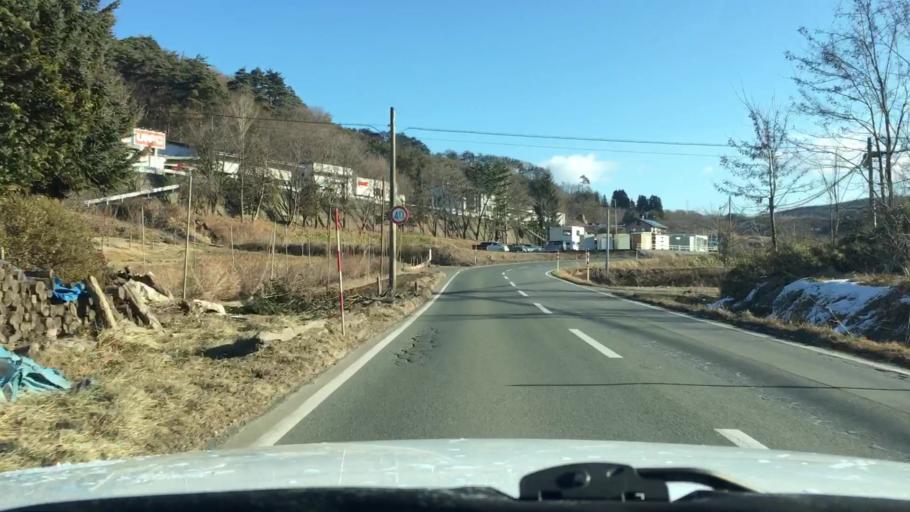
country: JP
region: Iwate
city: Morioka-shi
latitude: 39.6612
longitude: 141.1955
